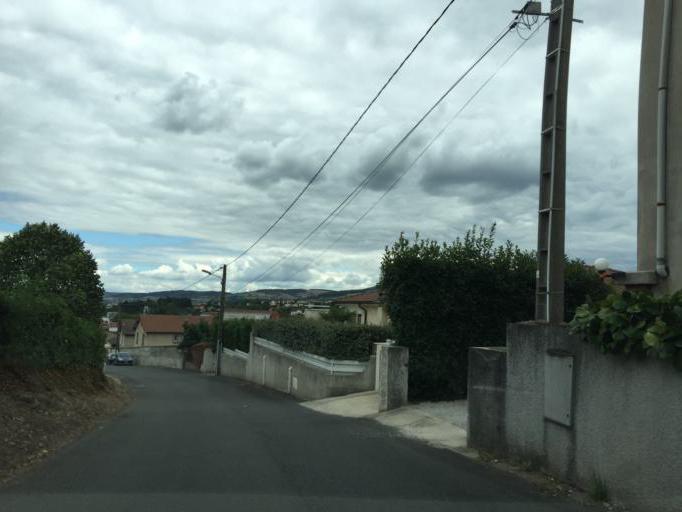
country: FR
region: Rhone-Alpes
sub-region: Departement de la Loire
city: Saint-Chamond
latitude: 45.4804
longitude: 4.5208
